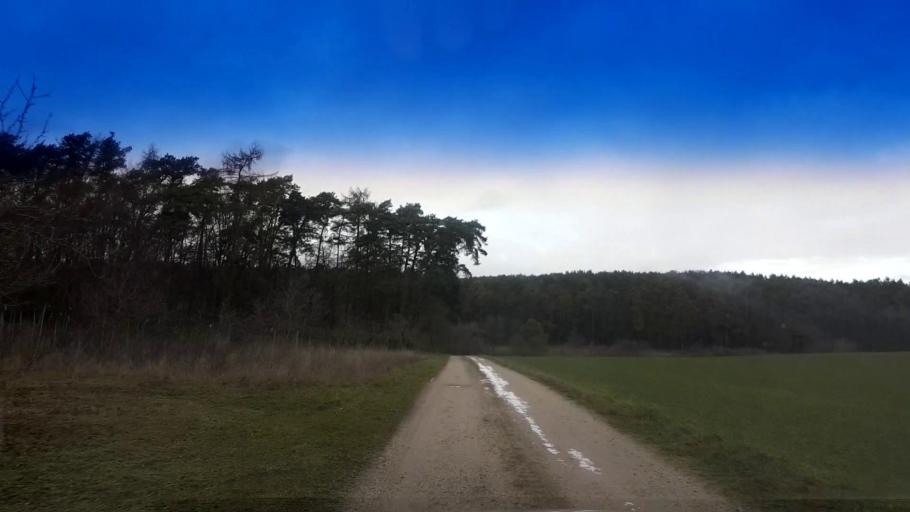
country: DE
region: Bavaria
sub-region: Upper Franconia
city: Lauter
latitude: 49.9545
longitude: 10.7709
